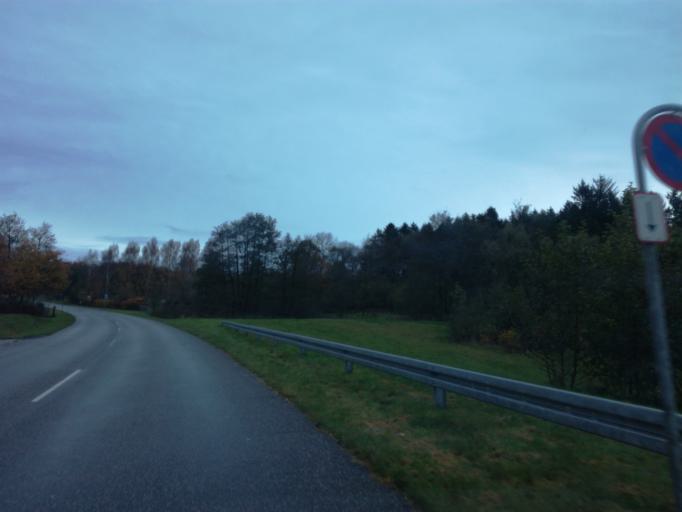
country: DK
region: South Denmark
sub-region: Vejle Kommune
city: Borkop
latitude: 55.6477
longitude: 9.6455
